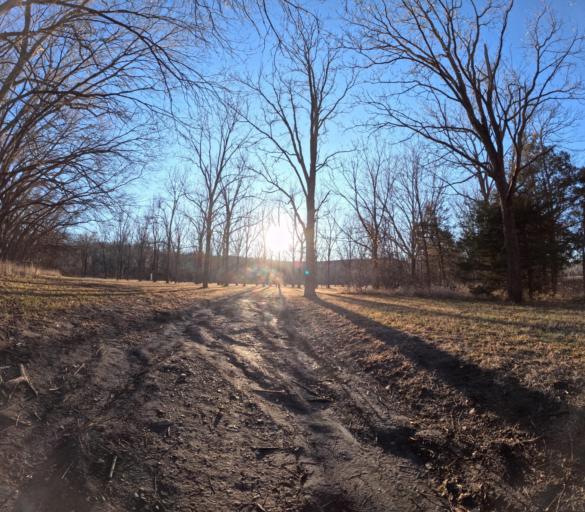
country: US
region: Kansas
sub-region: Riley County
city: Ogden
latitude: 39.2036
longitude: -96.6820
